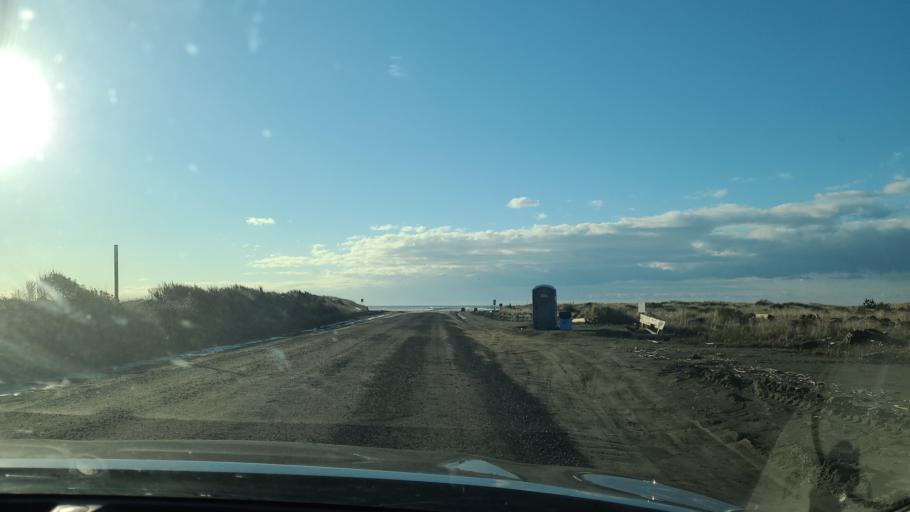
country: US
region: Washington
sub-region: Grays Harbor County
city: Ocean Shores
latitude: 46.9939
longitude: -124.1702
